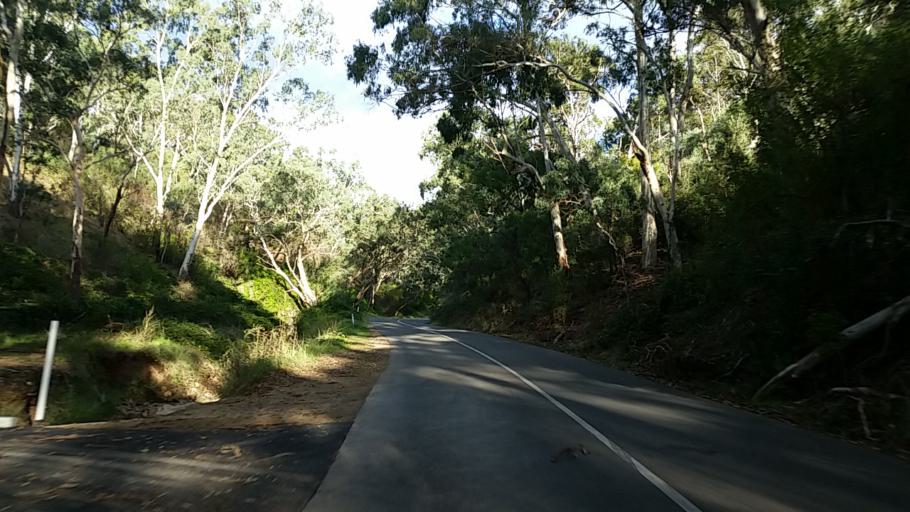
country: AU
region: South Australia
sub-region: Adelaide Hills
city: Adelaide Hills
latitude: -34.8904
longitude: 138.7280
